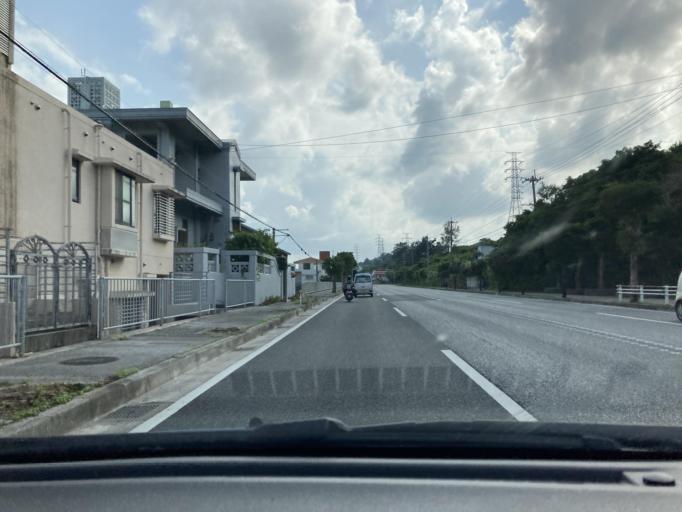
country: JP
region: Okinawa
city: Ginowan
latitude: 26.2591
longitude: 127.7865
